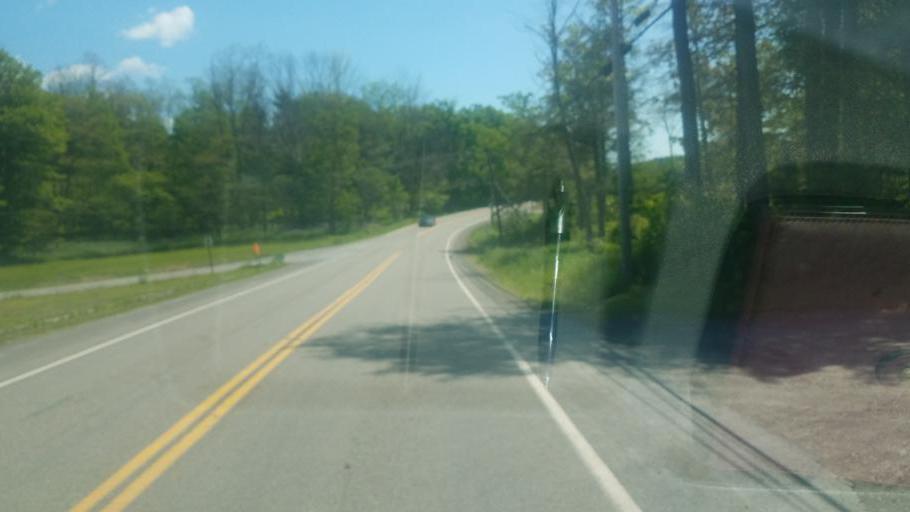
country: US
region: Pennsylvania
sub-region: Tioga County
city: Wellsboro
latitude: 41.7351
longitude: -77.3435
